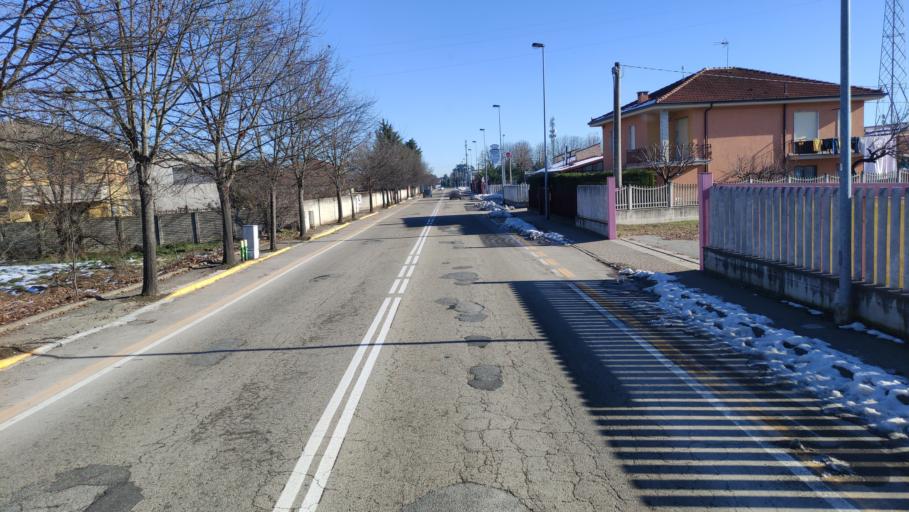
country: IT
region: Piedmont
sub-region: Provincia di Cuneo
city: Bra
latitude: 44.6873
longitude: 7.8387
